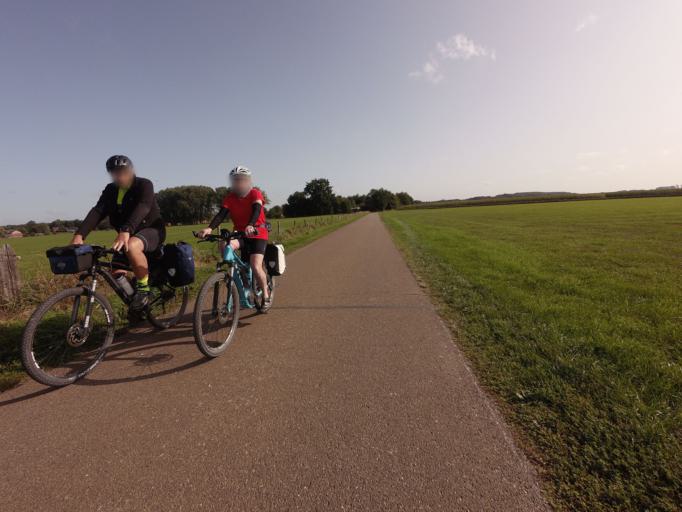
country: NL
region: Limburg
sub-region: Gemeente Roerdalen
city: Melick
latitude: 51.1519
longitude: 6.0183
